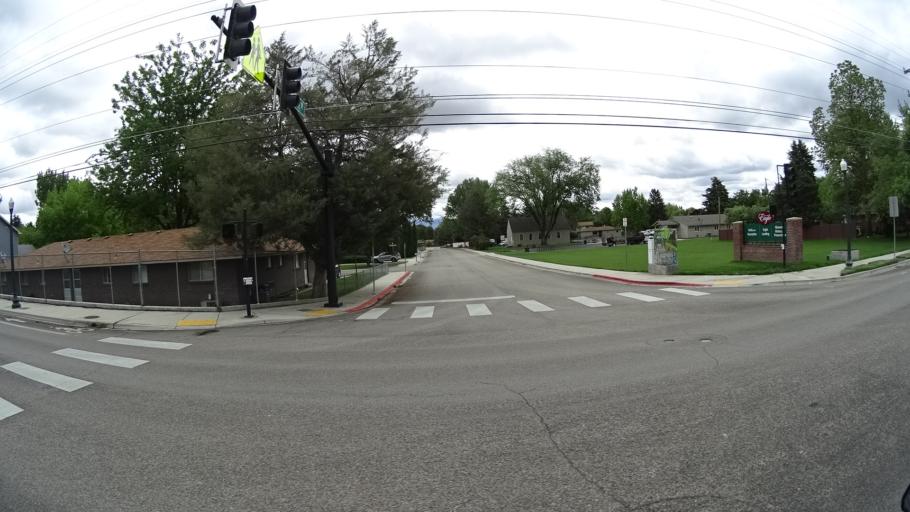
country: US
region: Idaho
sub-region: Ada County
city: Eagle
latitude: 43.6983
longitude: -116.3540
